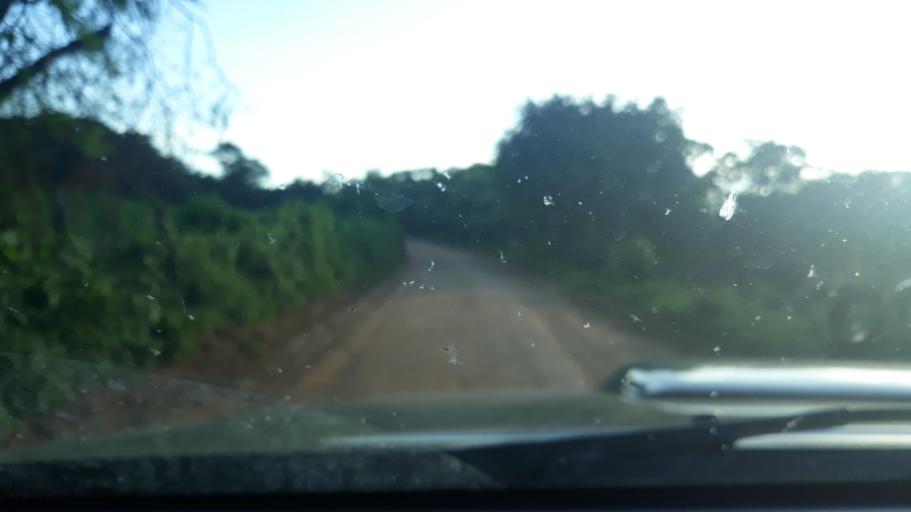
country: BR
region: Bahia
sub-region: Riacho De Santana
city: Riacho de Santana
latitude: -13.8294
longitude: -42.7294
